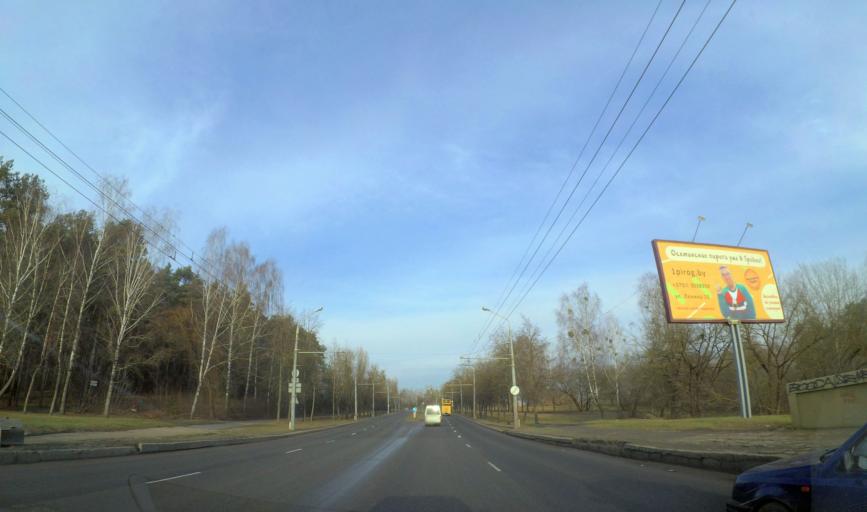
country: BY
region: Grodnenskaya
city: Hrodna
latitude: 53.6804
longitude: 23.8067
